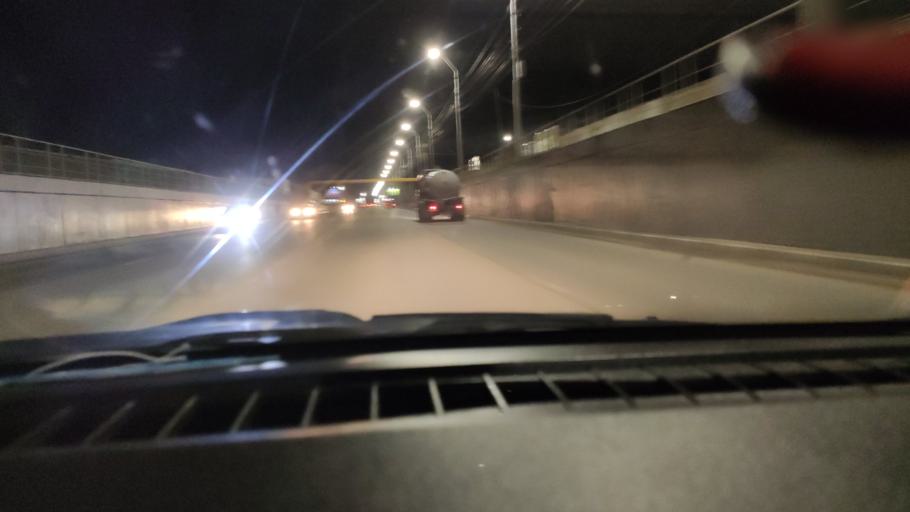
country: RU
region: Saratov
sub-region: Saratovskiy Rayon
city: Saratov
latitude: 51.5577
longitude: 46.0608
